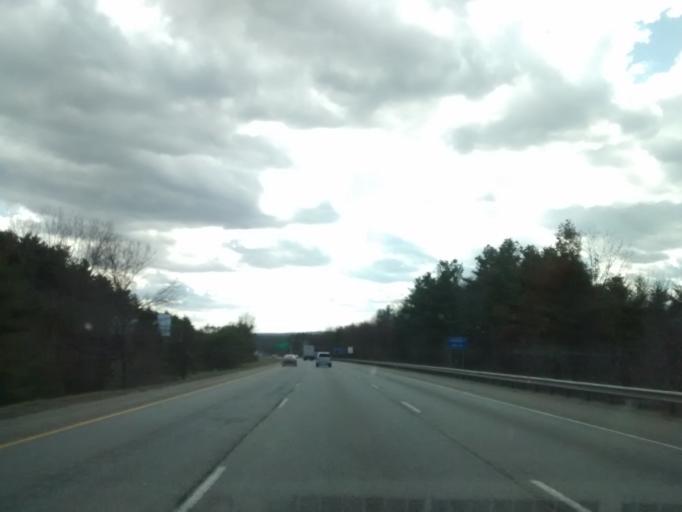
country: US
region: Massachusetts
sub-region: Worcester County
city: Berlin
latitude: 42.3599
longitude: -71.6011
